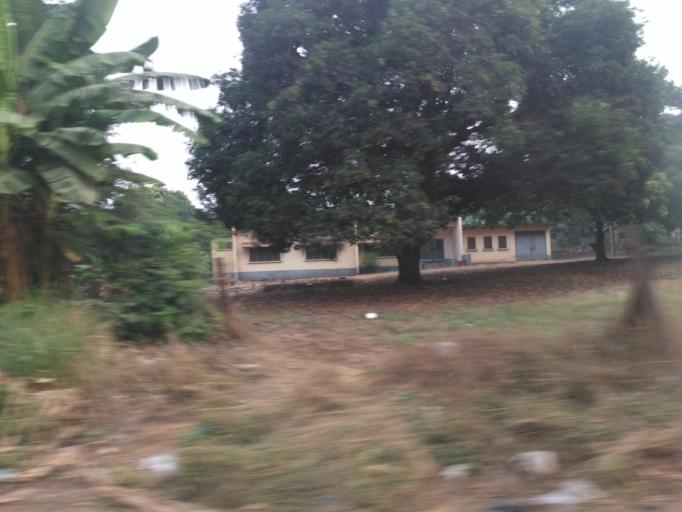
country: GH
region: Ashanti
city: Kumasi
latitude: 6.6824
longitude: -1.6180
